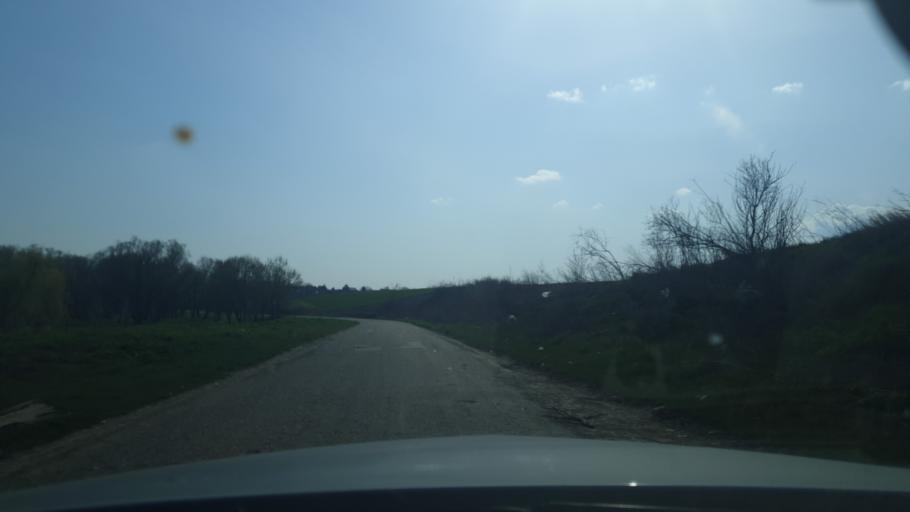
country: RS
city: Putinci
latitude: 45.0121
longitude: 19.9429
